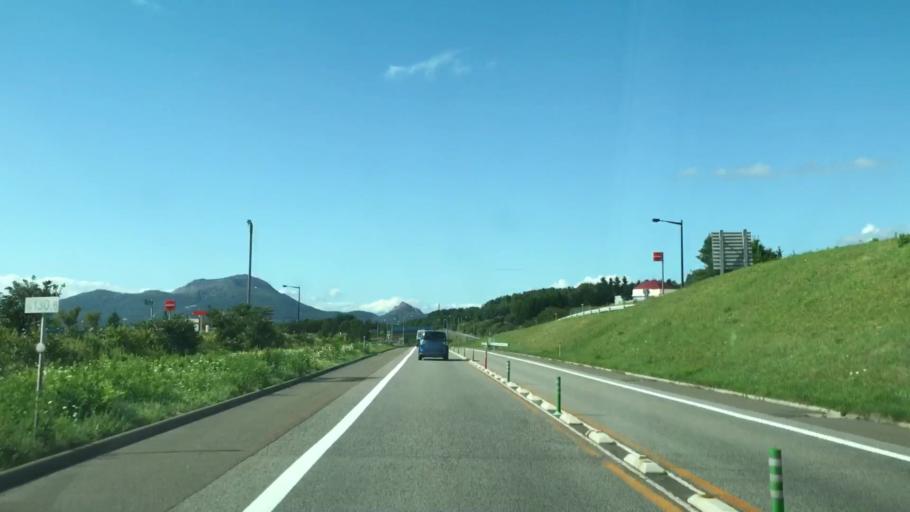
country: JP
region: Hokkaido
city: Date
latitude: 42.4653
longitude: 140.9093
